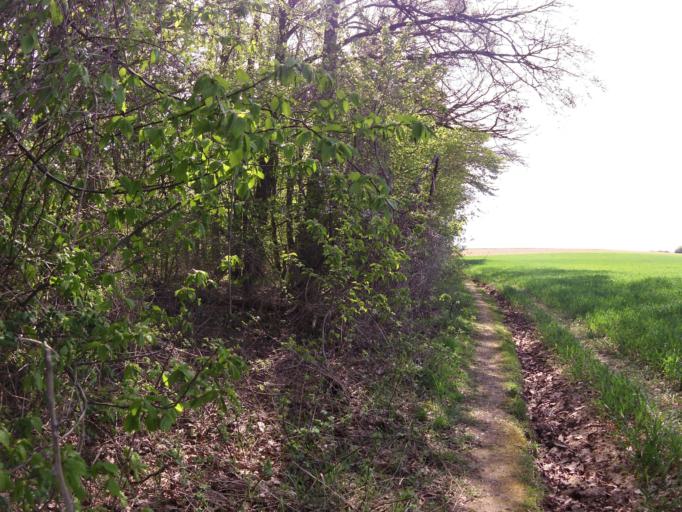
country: DE
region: Bavaria
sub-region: Regierungsbezirk Unterfranken
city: Rimpar
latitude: 49.8623
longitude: 9.9793
